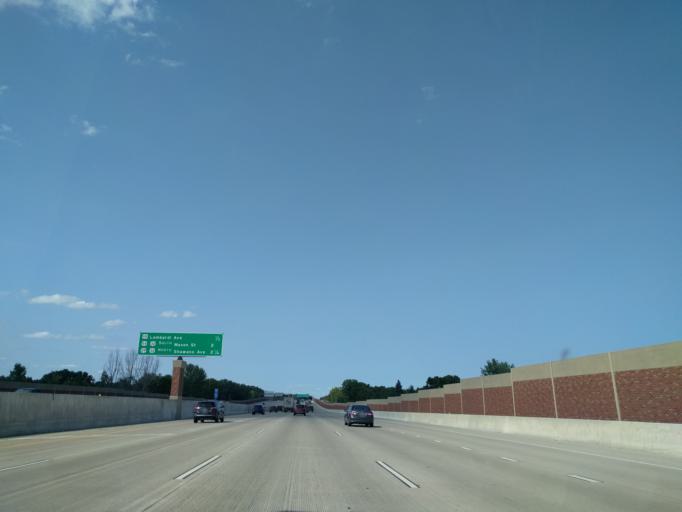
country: US
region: Wisconsin
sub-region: Brown County
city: Ashwaubenon
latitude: 44.4973
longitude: -88.0815
